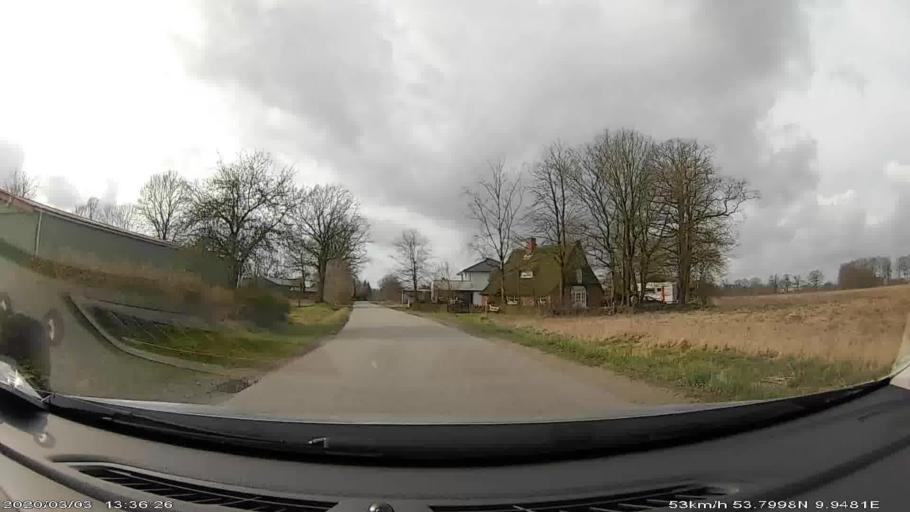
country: DE
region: Schleswig-Holstein
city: Alveslohe
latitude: 53.7999
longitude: 9.9466
